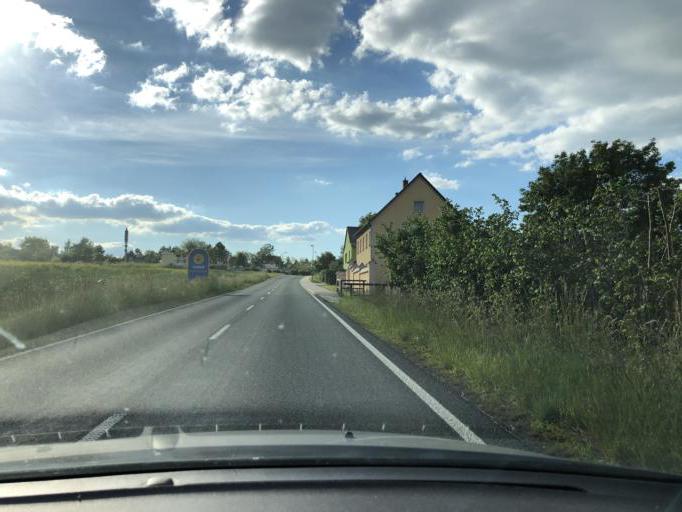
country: DE
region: Thuringia
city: Schmolln
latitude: 50.8912
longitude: 12.3672
